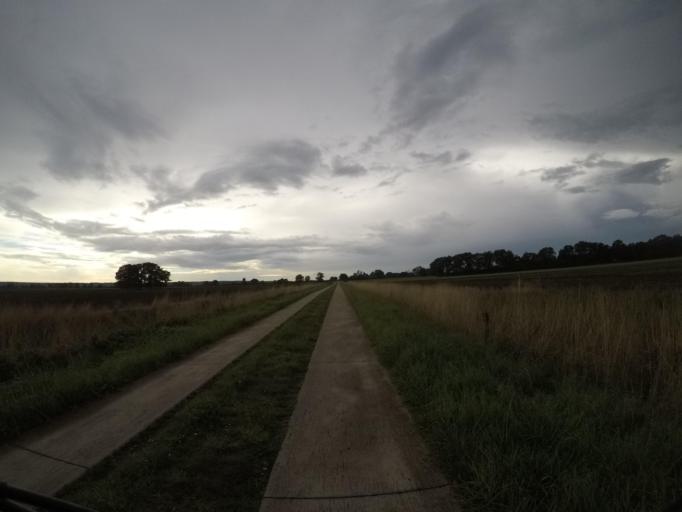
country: DE
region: Lower Saxony
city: Neu Darchau
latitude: 53.2645
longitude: 10.8906
